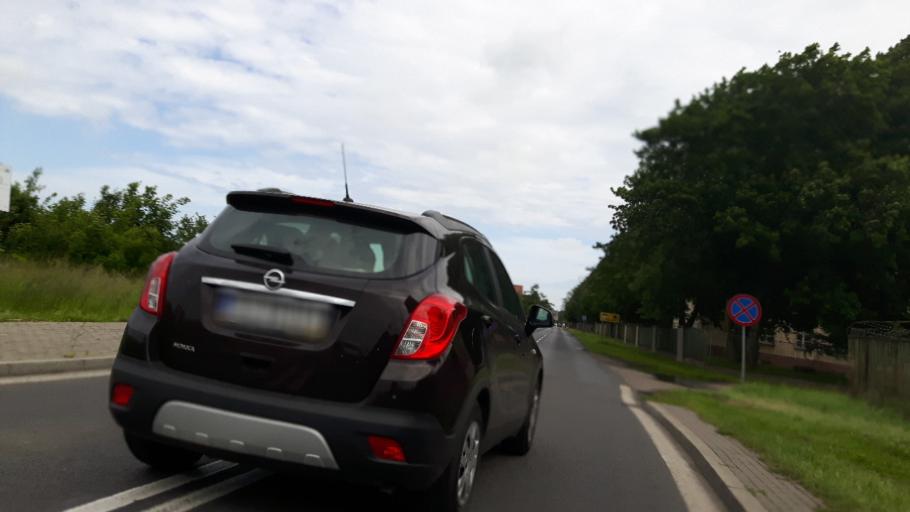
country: PL
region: West Pomeranian Voivodeship
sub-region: Powiat gryficki
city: Trzebiatow
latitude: 54.0507
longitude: 15.2554
